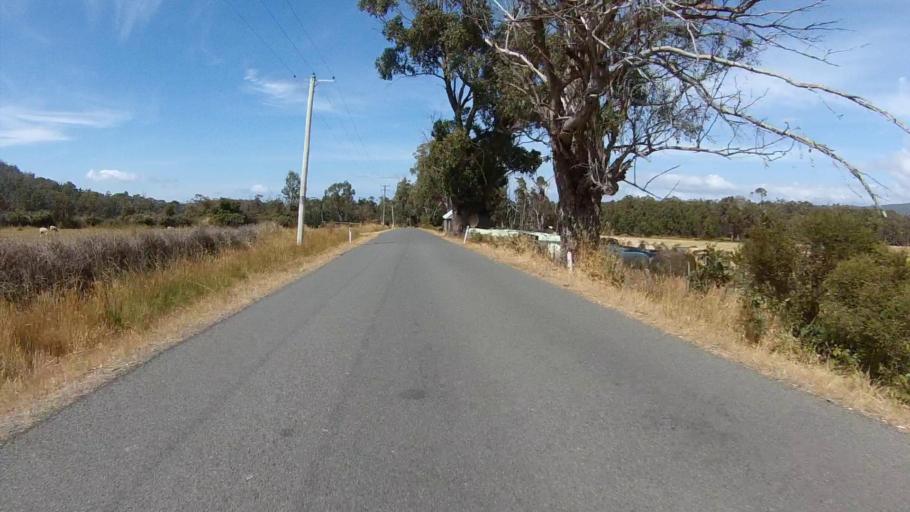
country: AU
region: Tasmania
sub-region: Huon Valley
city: Cygnet
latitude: -43.2369
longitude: 147.1251
